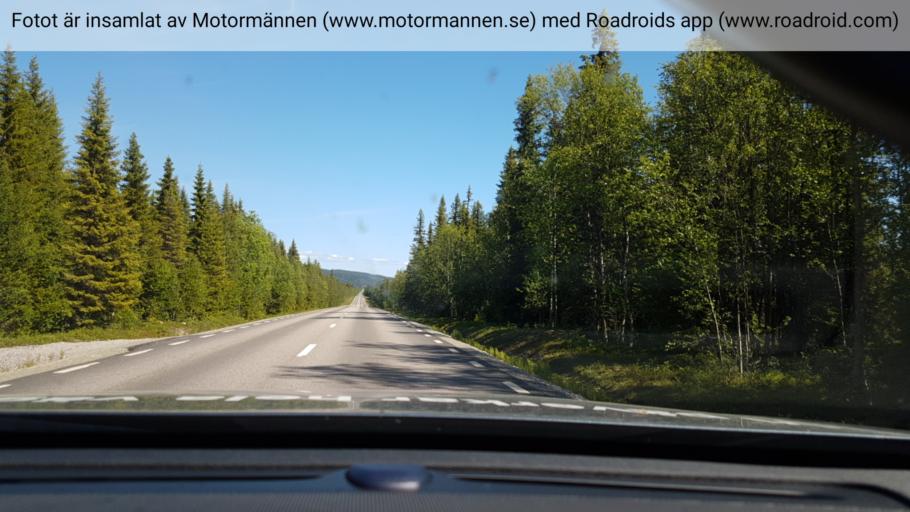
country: SE
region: Vaesterbotten
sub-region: Asele Kommun
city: Insjon
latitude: 64.7277
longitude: 17.5599
